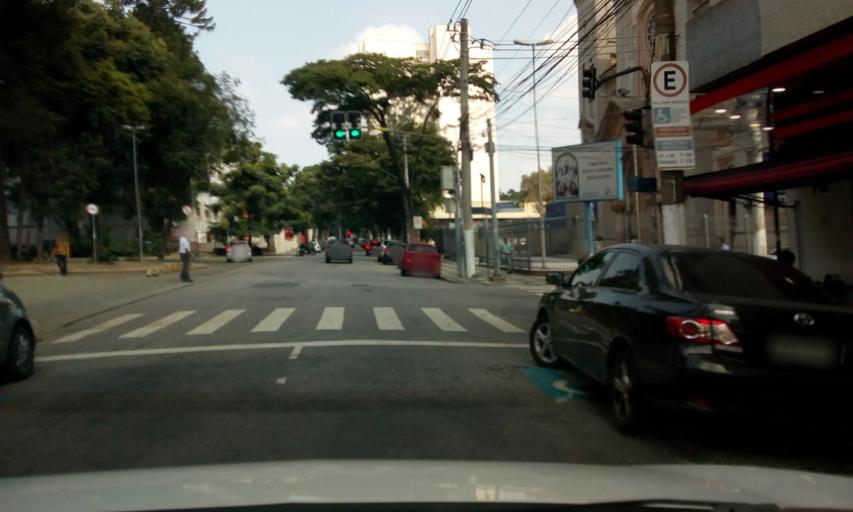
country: BR
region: Sao Paulo
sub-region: Sao Paulo
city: Sao Paulo
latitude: -23.5297
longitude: -46.6341
